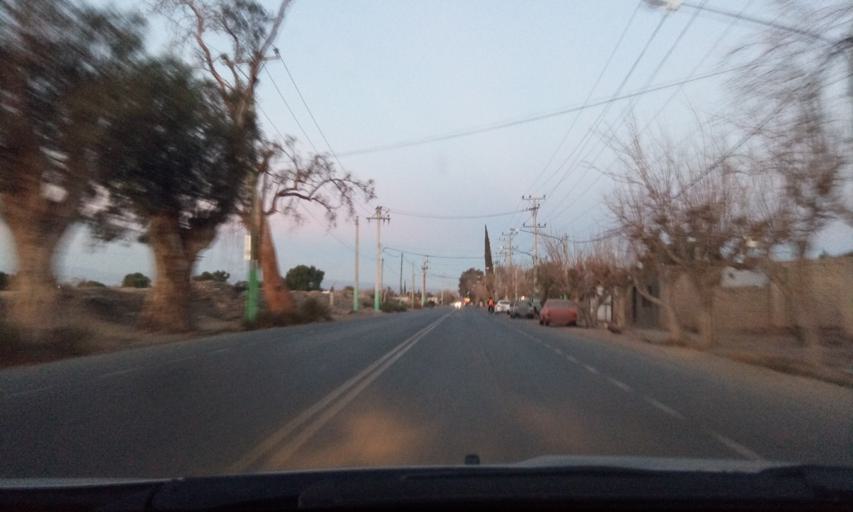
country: AR
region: San Juan
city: San Juan
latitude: -31.5500
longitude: -68.5712
